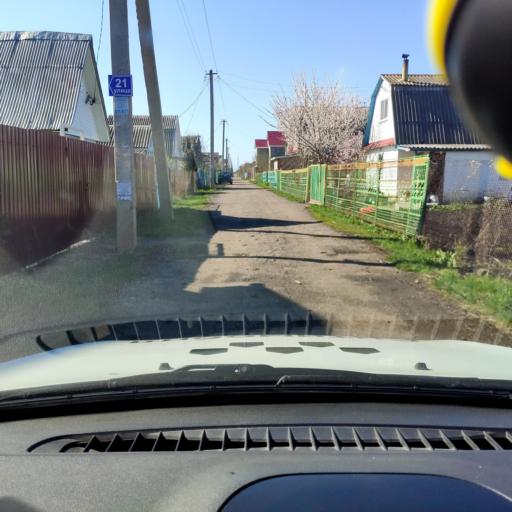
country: RU
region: Samara
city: Tol'yatti
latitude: 53.5996
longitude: 49.2954
